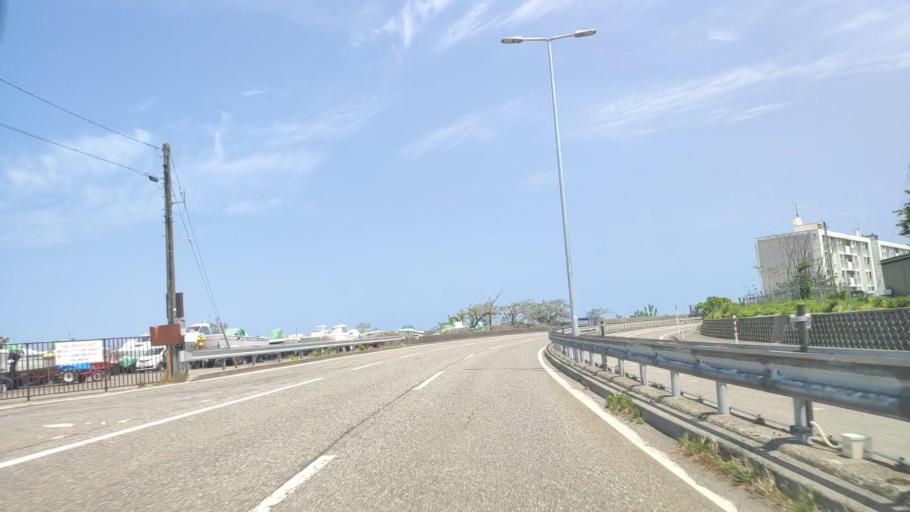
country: JP
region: Niigata
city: Itoigawa
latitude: 37.0436
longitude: 137.8465
